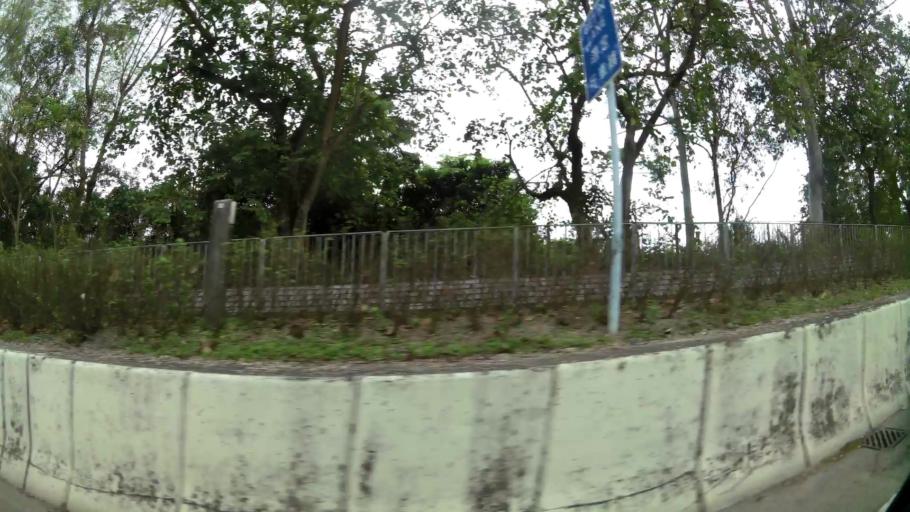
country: HK
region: Wong Tai Sin
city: Wong Tai Sin
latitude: 22.3426
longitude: 114.1705
